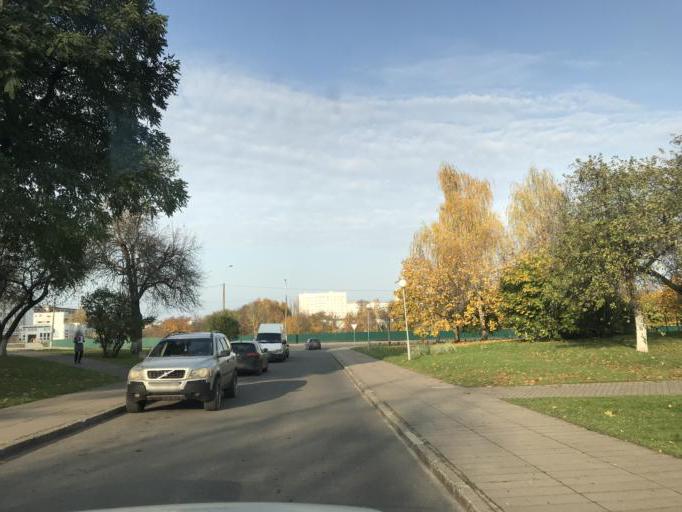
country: BY
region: Mogilev
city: Mahilyow
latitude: 53.9073
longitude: 30.3497
